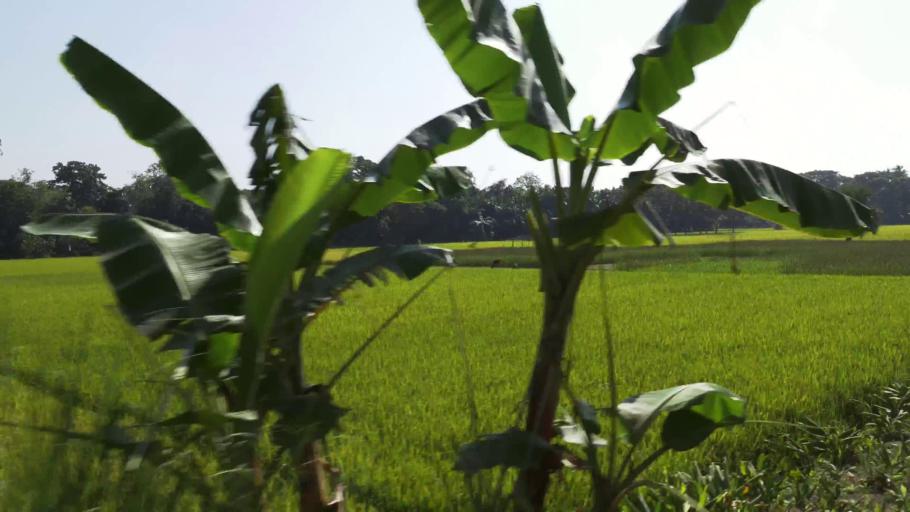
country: BD
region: Dhaka
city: Gafargaon
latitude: 24.5086
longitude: 90.5157
